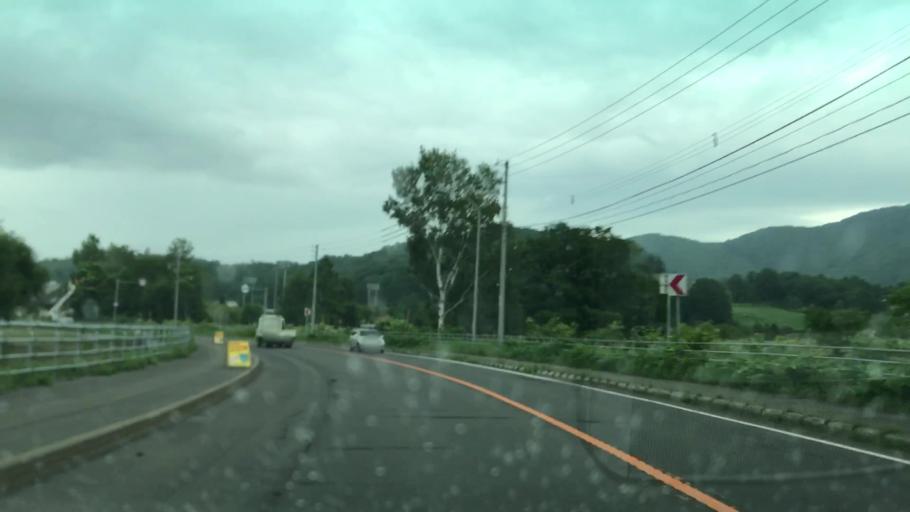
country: JP
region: Hokkaido
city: Niseko Town
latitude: 42.8096
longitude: 140.5390
